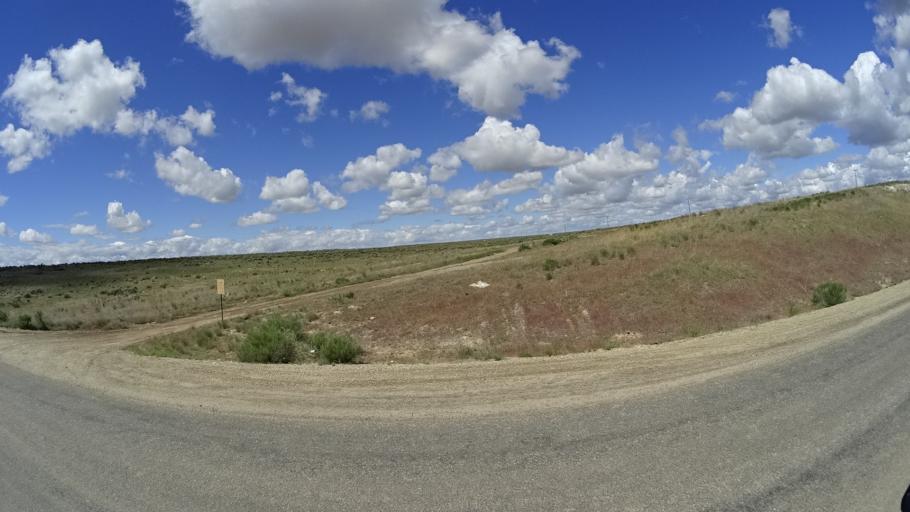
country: US
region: Idaho
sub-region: Ada County
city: Garden City
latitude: 43.4871
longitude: -116.2743
